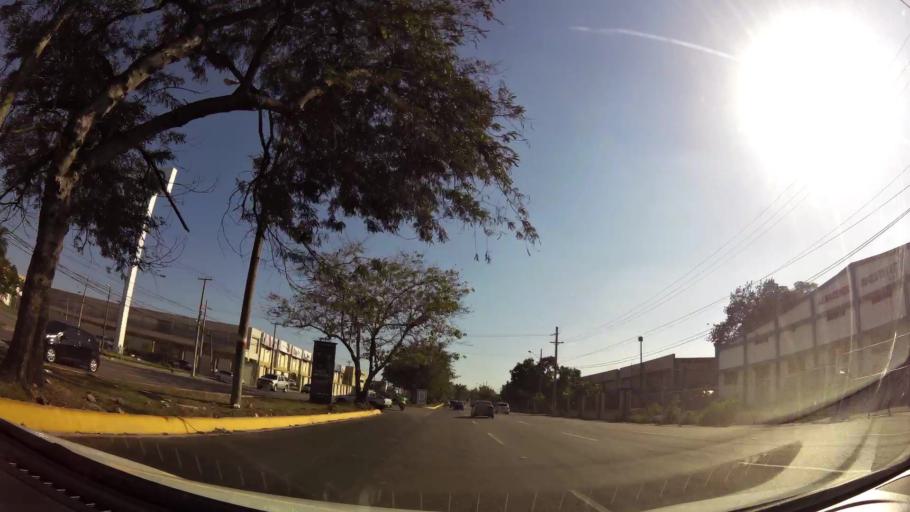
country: DO
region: Nacional
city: Bella Vista
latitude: 18.4569
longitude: -69.9712
